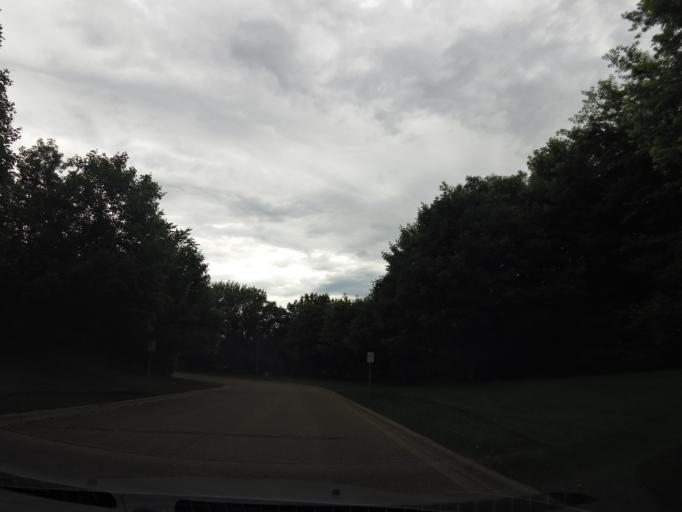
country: US
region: Minnesota
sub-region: Scott County
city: Prior Lake
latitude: 44.6974
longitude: -93.4241
